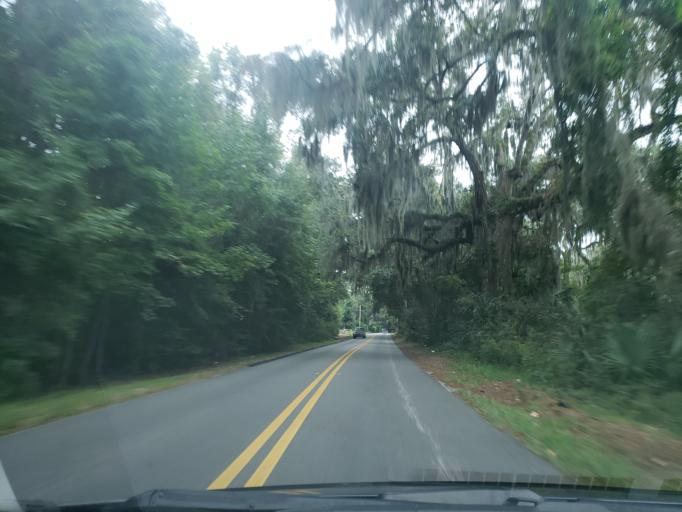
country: US
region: Georgia
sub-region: Chatham County
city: Montgomery
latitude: 31.9634
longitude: -81.1009
